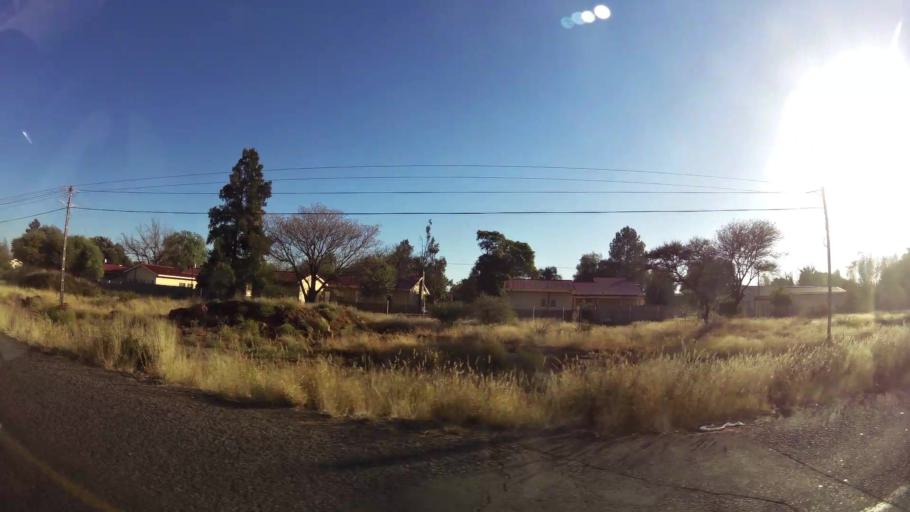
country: ZA
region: Northern Cape
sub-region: Frances Baard District Municipality
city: Kimberley
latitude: -28.7430
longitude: 24.7231
